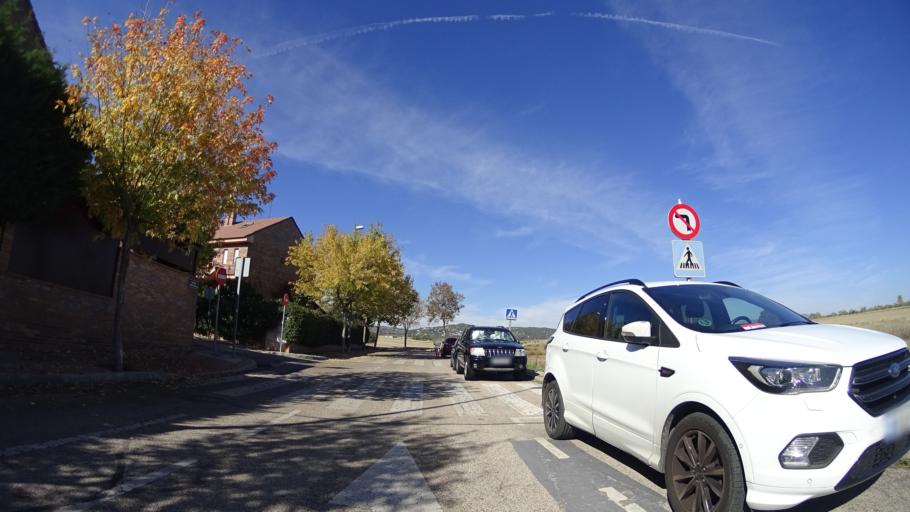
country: ES
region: Madrid
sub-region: Provincia de Madrid
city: Villanueva del Pardillo
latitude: 40.5023
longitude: -3.9667
